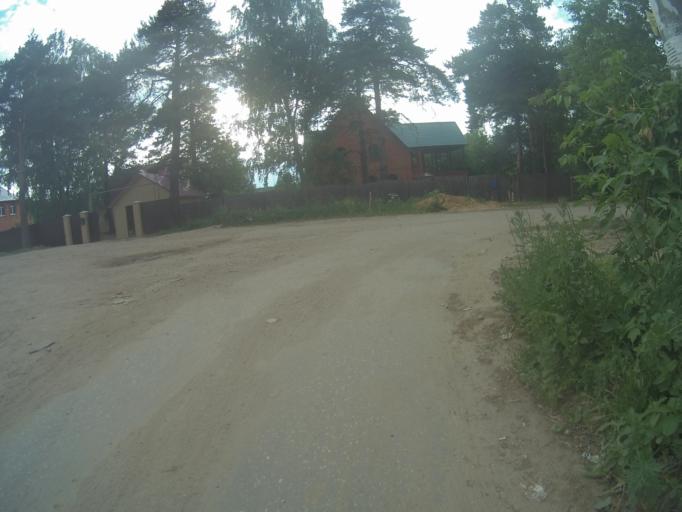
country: RU
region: Vladimir
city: Vladimir
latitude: 56.2197
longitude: 40.4067
